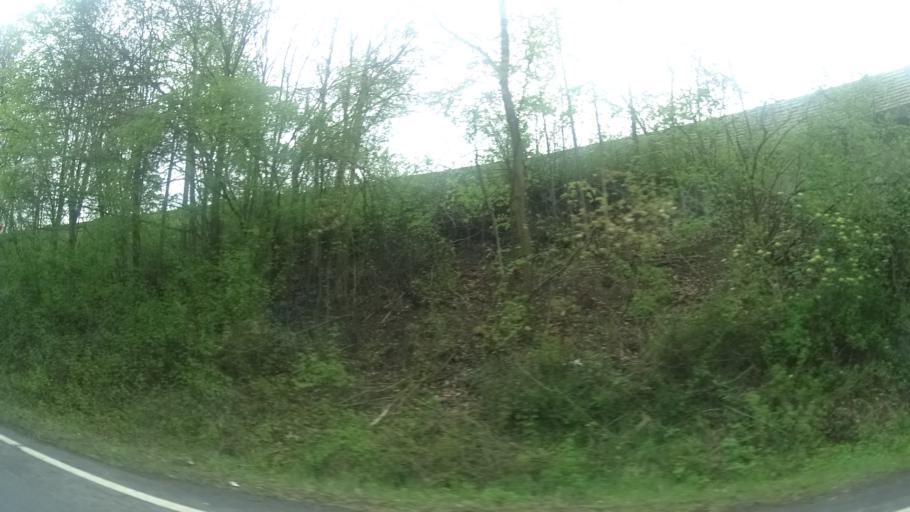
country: DE
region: Hesse
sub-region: Regierungsbezirk Giessen
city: Giessen
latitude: 50.5634
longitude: 8.6579
